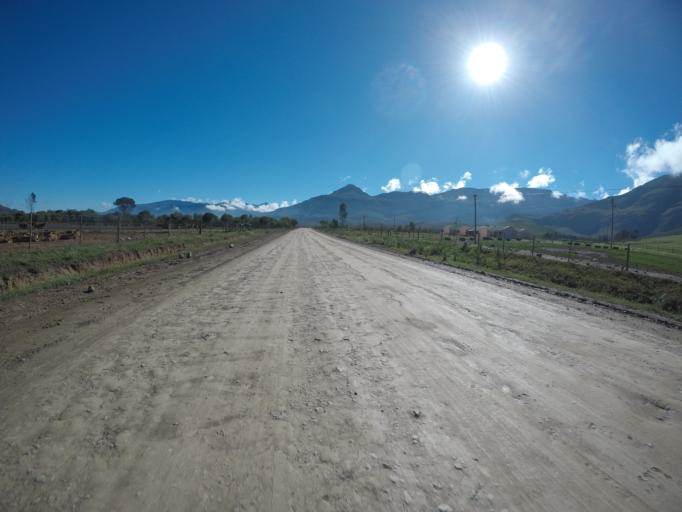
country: ZA
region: Western Cape
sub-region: Overberg District Municipality
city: Caledon
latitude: -34.0685
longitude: 19.6310
